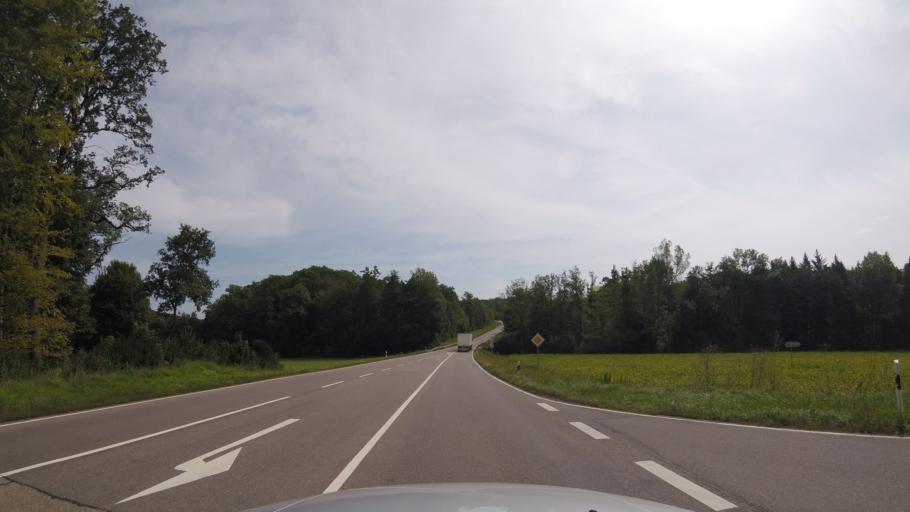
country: DE
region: Baden-Wuerttemberg
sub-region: Regierungsbezirk Stuttgart
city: Grossbottwar
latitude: 48.9844
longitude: 9.3190
